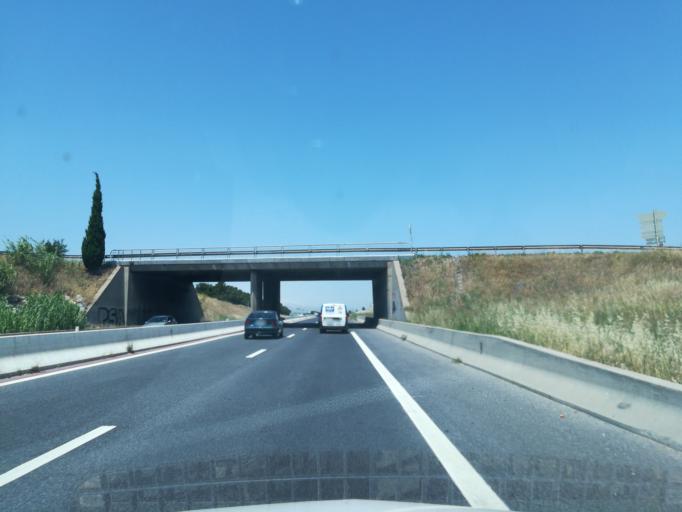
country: FR
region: Languedoc-Roussillon
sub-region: Departement des Pyrenees-Orientales
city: Perpignan
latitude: 42.7266
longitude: 2.8788
